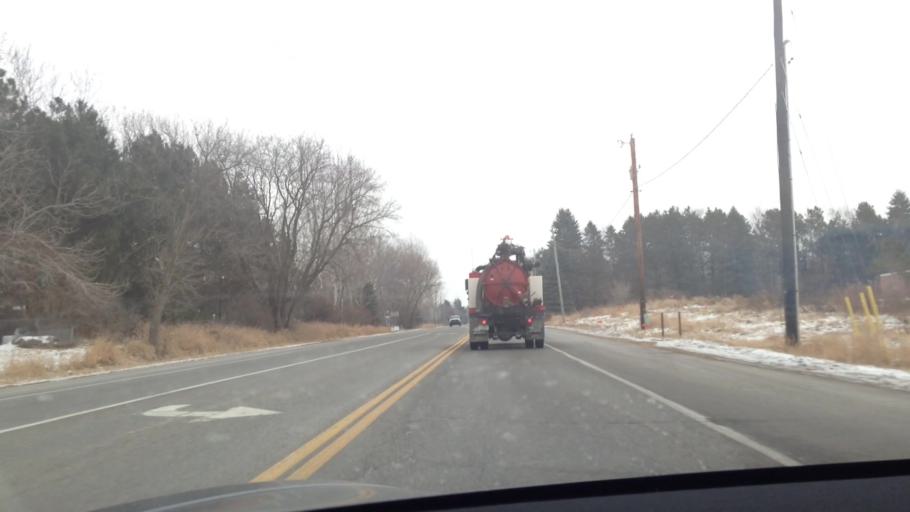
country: US
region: Minnesota
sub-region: Washington County
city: Forest Lake
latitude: 45.2523
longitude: -93.0090
